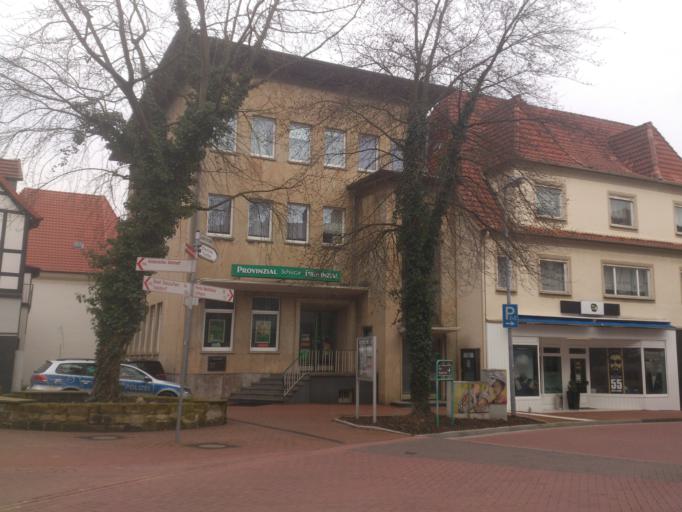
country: DE
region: North Rhine-Westphalia
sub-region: Regierungsbezirk Detmold
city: Vlotho
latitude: 52.1678
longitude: 8.8616
